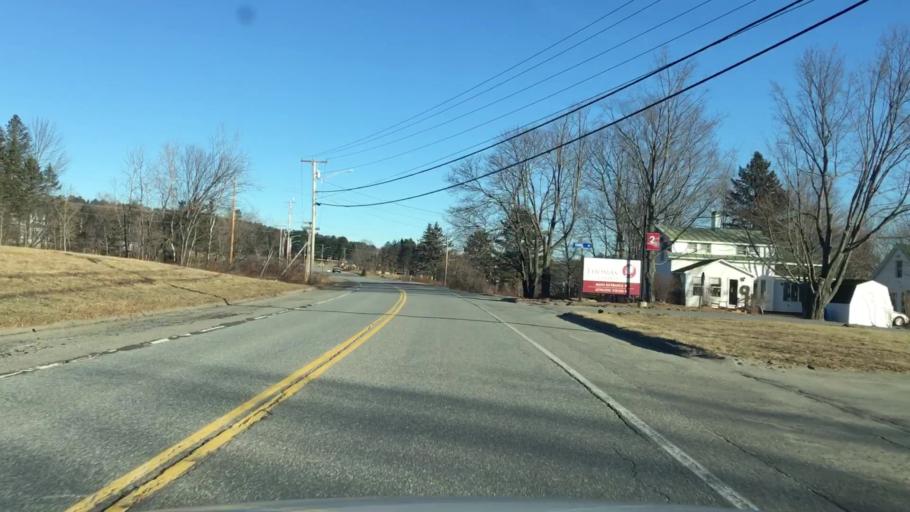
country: US
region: Maine
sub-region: Kennebec County
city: Waterville
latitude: 44.5224
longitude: -69.6672
